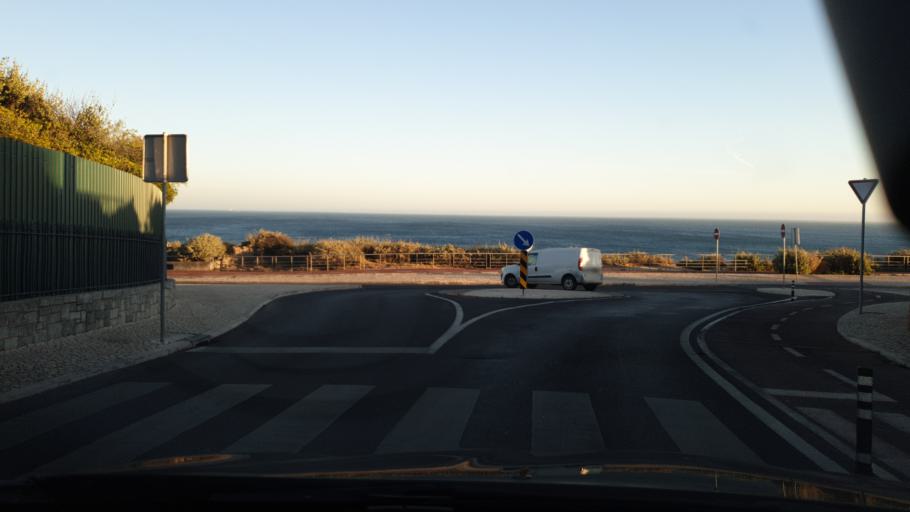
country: PT
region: Lisbon
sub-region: Cascais
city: Cascais
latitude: 38.6923
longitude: -9.4311
